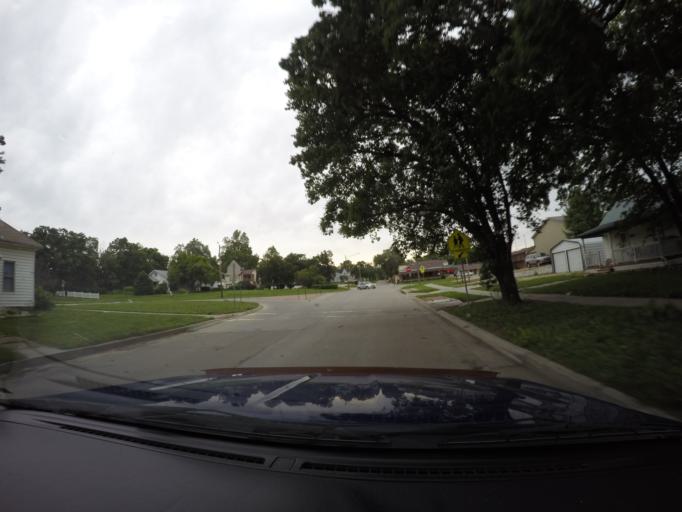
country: US
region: Kansas
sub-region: Clay County
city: Clay Center
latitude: 39.3800
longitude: -97.1192
